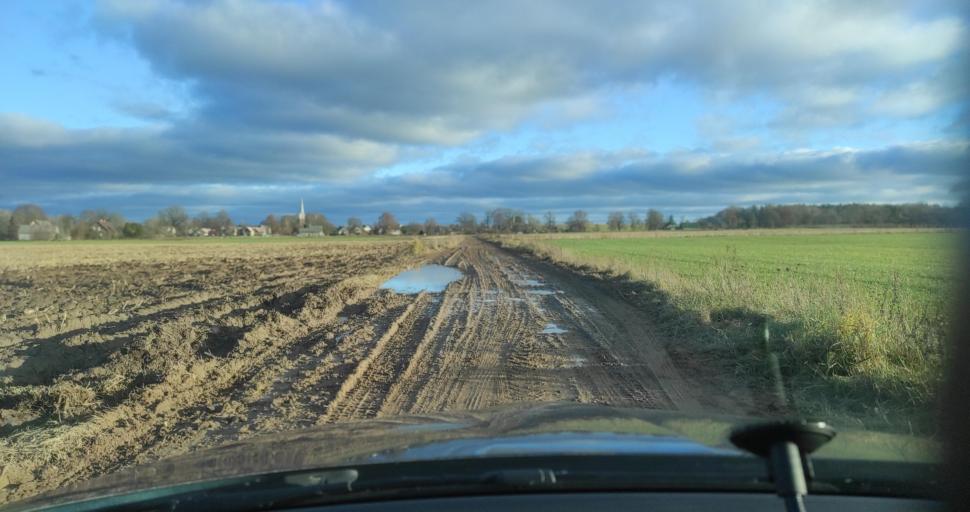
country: LV
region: Kuldigas Rajons
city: Kuldiga
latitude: 57.2700
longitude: 22.0234
